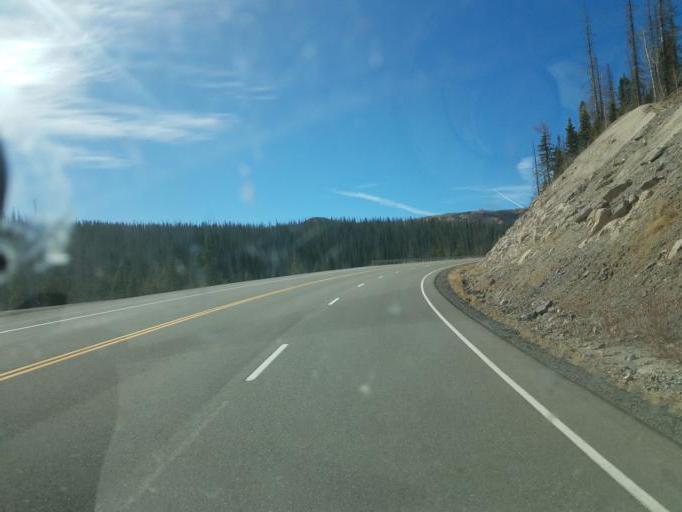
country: US
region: Colorado
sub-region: Archuleta County
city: Pagosa Springs
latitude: 37.4804
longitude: -106.7717
